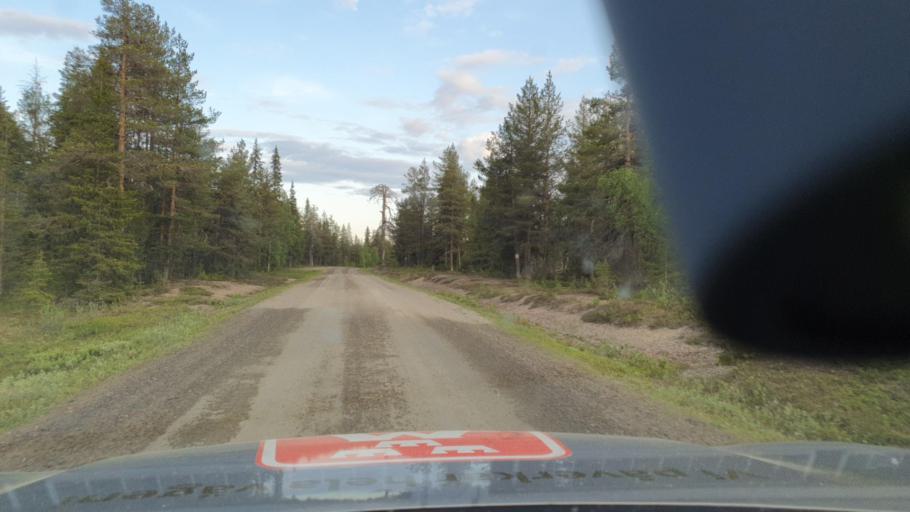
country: SE
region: Norrbotten
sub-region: Bodens Kommun
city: Boden
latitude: 66.5702
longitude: 21.4269
